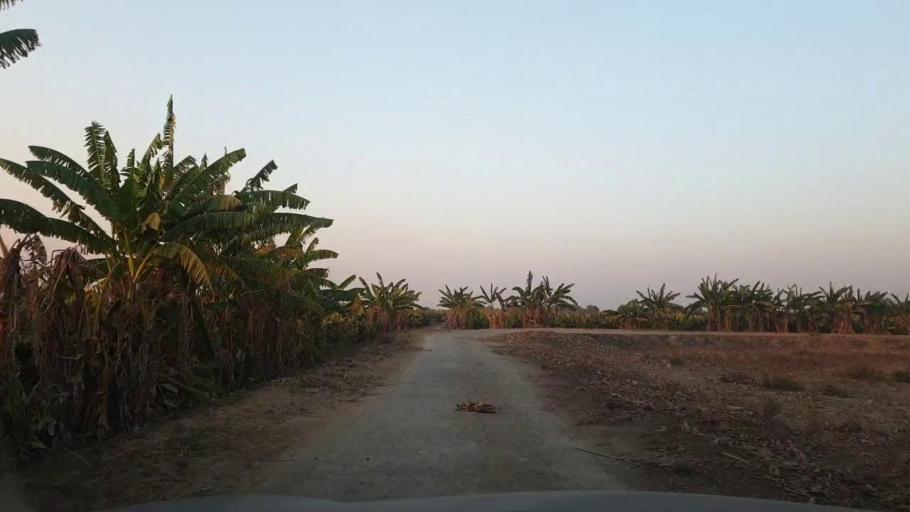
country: PK
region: Sindh
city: Mirpur Khas
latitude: 25.5956
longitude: 68.8504
